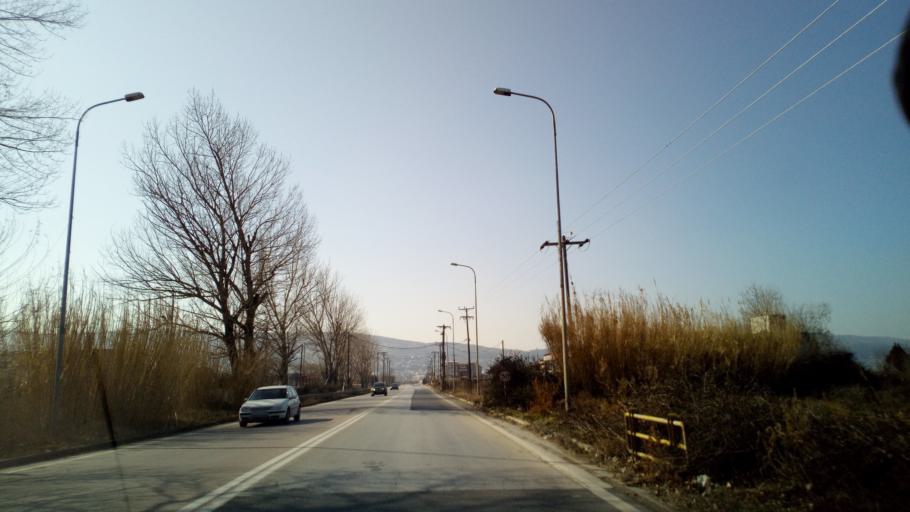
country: GR
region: Central Macedonia
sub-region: Nomos Thessalonikis
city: Lagyna
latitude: 40.7334
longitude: 23.0264
